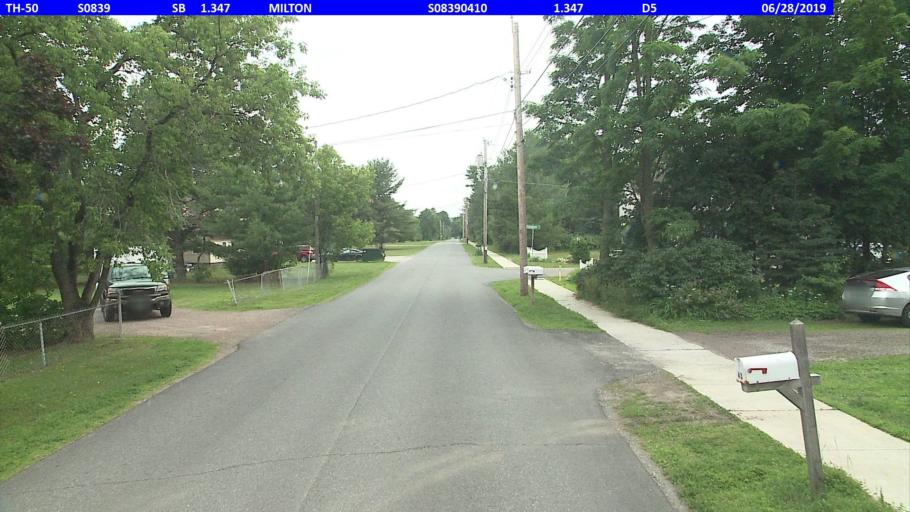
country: US
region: Vermont
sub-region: Chittenden County
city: Milton
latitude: 44.6228
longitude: -73.1117
